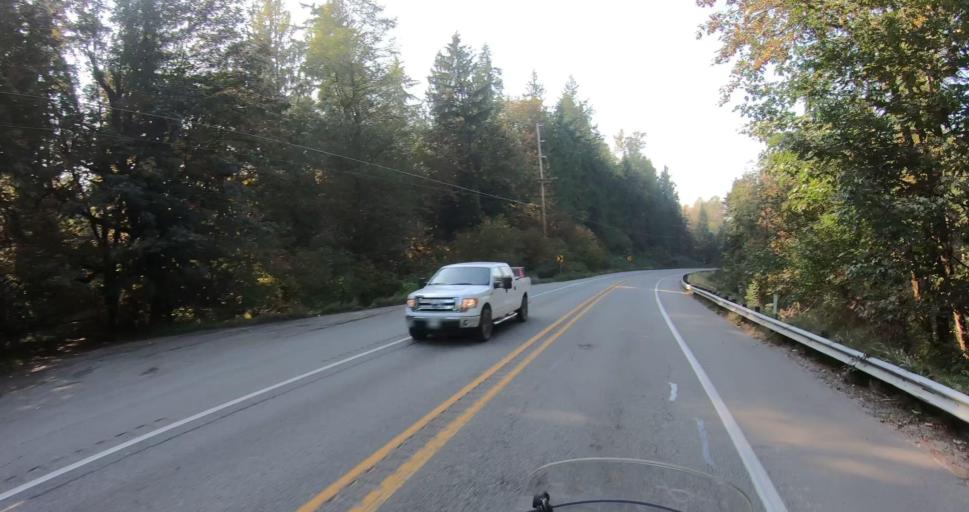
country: US
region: Washington
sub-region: King County
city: Black Diamond
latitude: 47.2671
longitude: -121.9902
